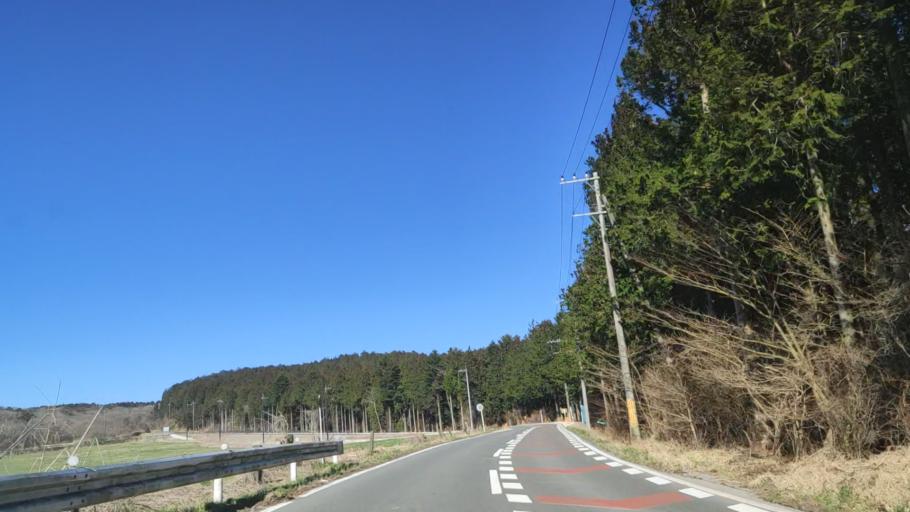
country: JP
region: Yamanashi
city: Fujikawaguchiko
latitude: 35.3816
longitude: 138.6040
